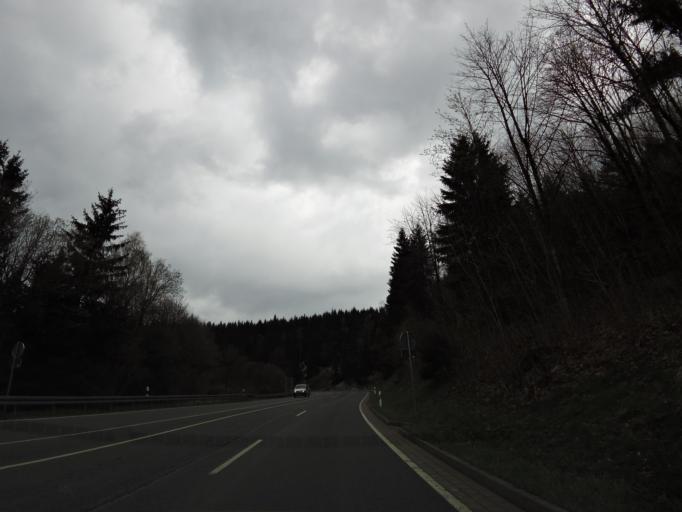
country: DE
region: Lower Saxony
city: Clausthal-Zellerfeld
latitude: 51.7641
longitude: 10.3050
